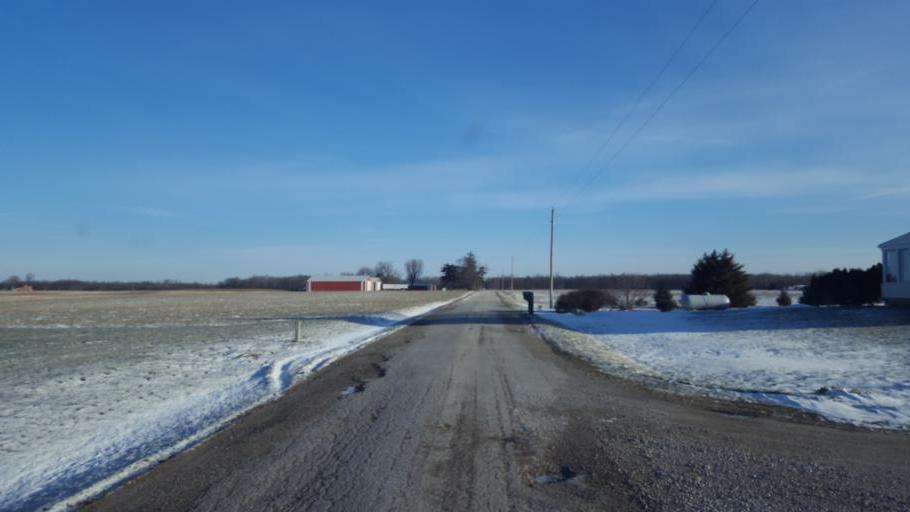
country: US
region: Ohio
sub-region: Morrow County
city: Mount Gilead
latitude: 40.6091
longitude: -82.8996
